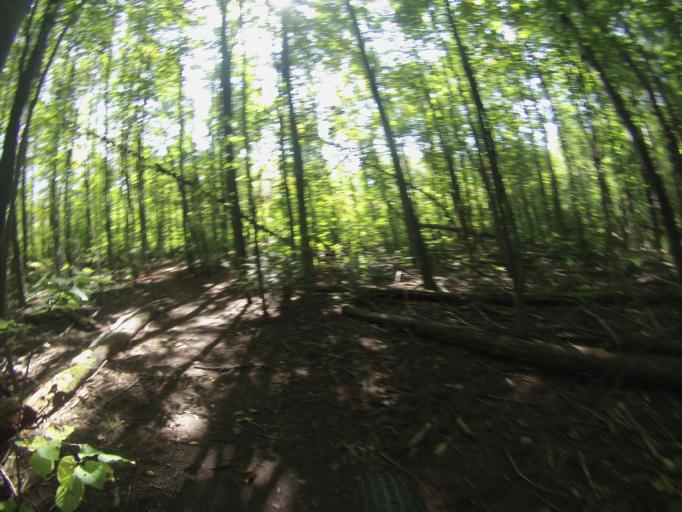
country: CA
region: Ontario
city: Ottawa
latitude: 45.3600
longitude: -75.6284
